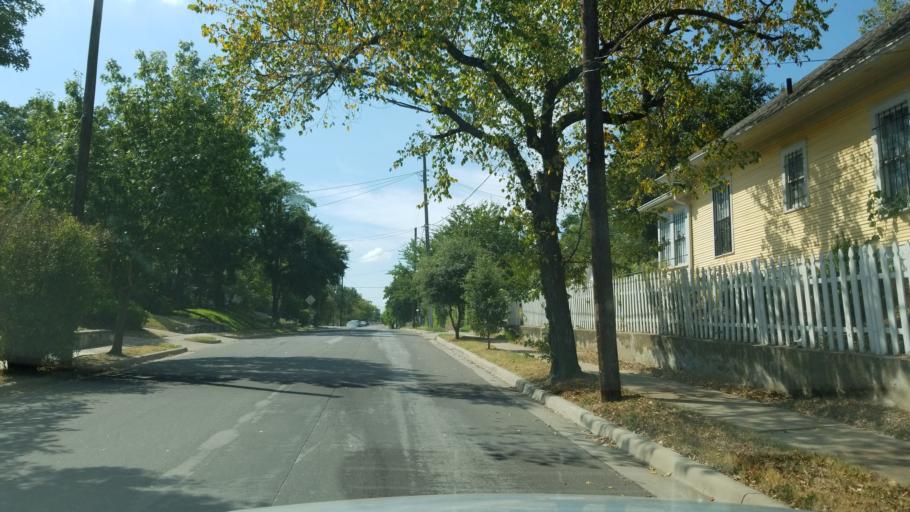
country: US
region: Texas
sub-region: Dallas County
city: Dallas
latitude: 32.7537
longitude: -96.8191
